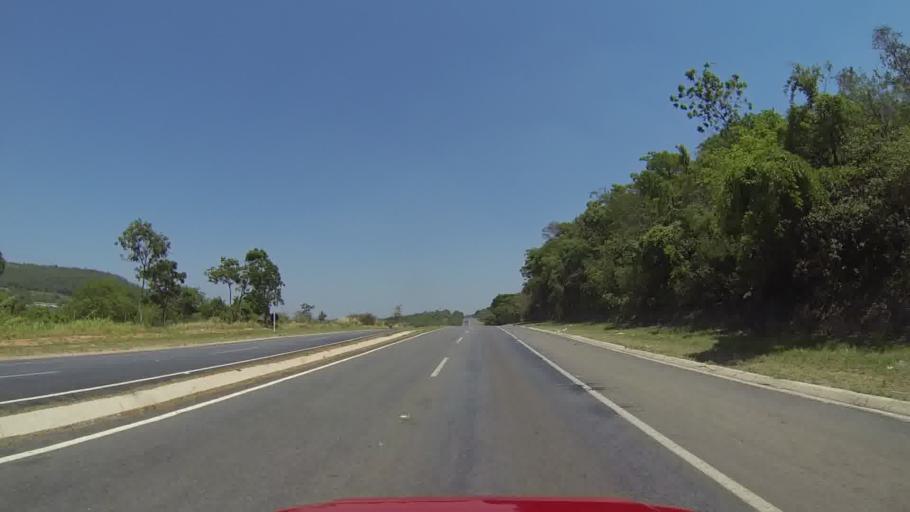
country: BR
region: Minas Gerais
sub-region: Itauna
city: Itauna
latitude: -20.0635
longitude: -44.5848
